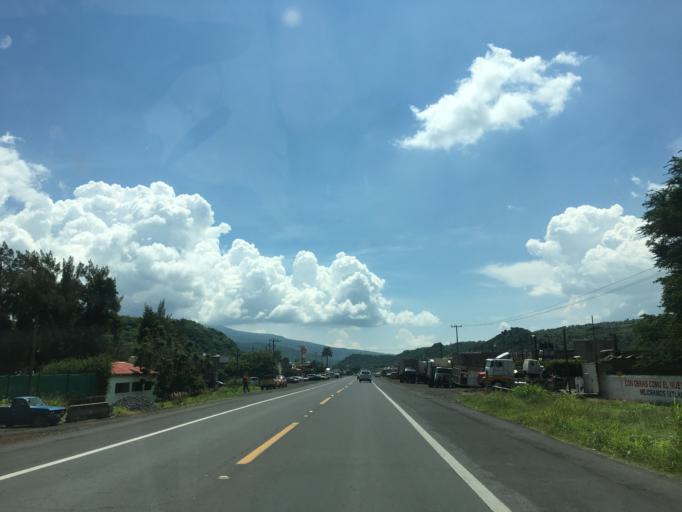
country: MX
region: Nayarit
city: Ixtlan del Rio
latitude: 21.0369
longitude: -104.3971
